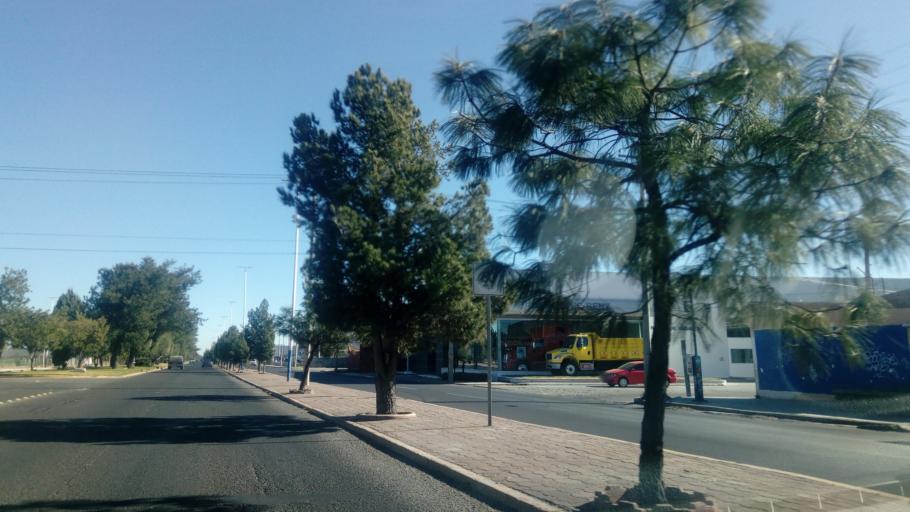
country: MX
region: Durango
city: Victoria de Durango
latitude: 24.0510
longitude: -104.6190
